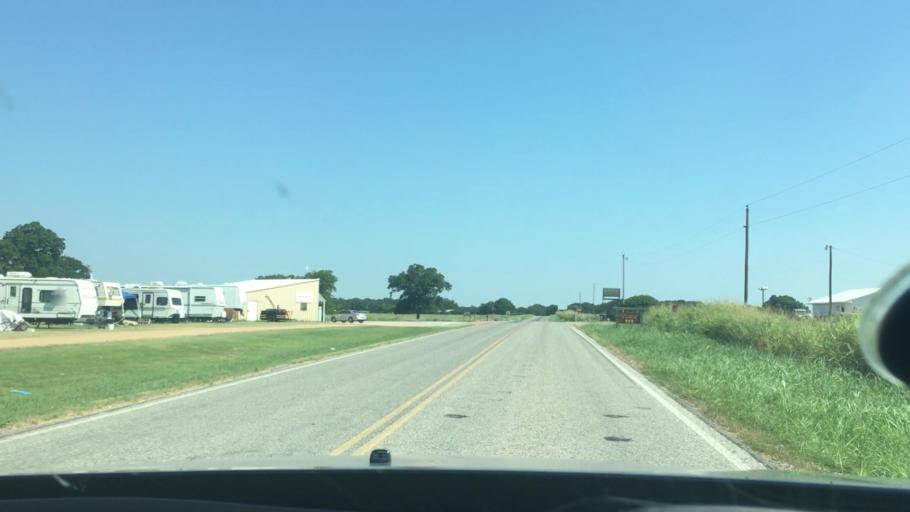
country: US
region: Oklahoma
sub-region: Johnston County
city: Tishomingo
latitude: 34.3090
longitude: -96.6184
